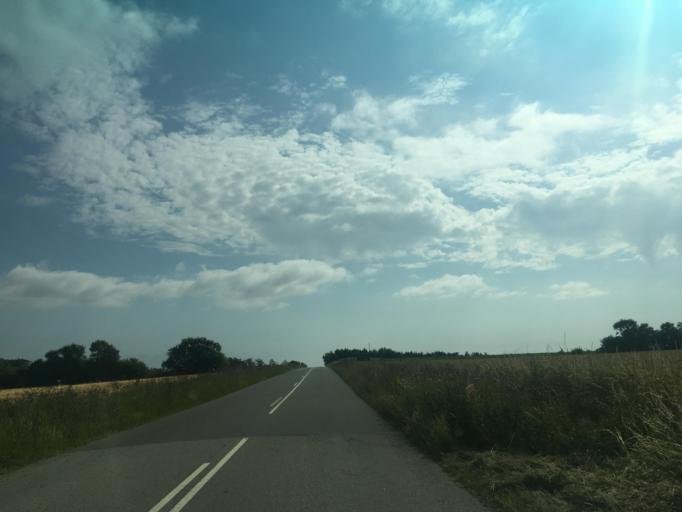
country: DK
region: North Denmark
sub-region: Thisted Kommune
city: Thisted
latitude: 56.8522
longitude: 8.6021
